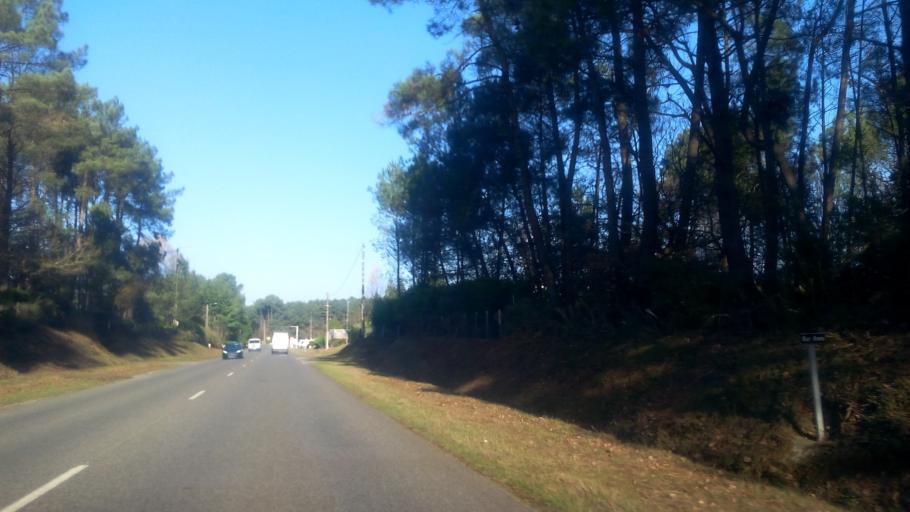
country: FR
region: Brittany
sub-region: Departement du Morbihan
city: Saint-Vincent-sur-Oust
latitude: 47.6871
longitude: -2.1394
